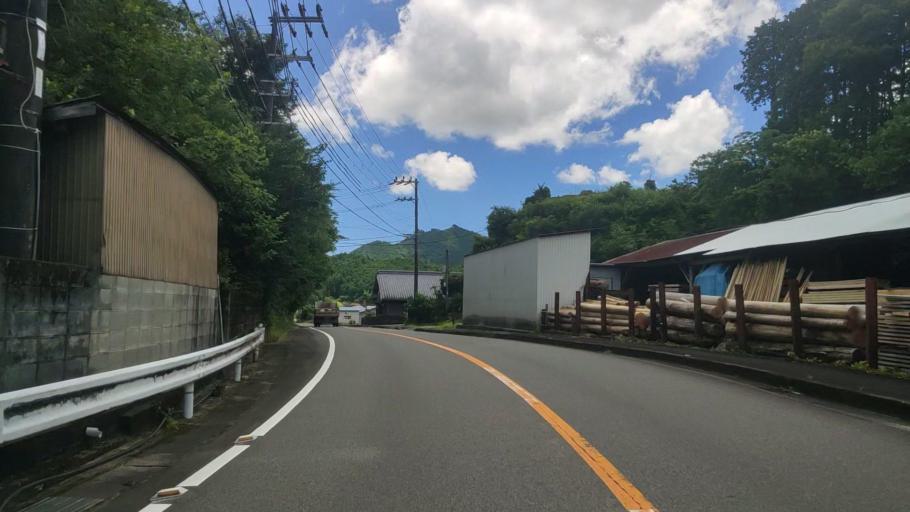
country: JP
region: Mie
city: Owase
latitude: 33.9506
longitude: 136.0699
